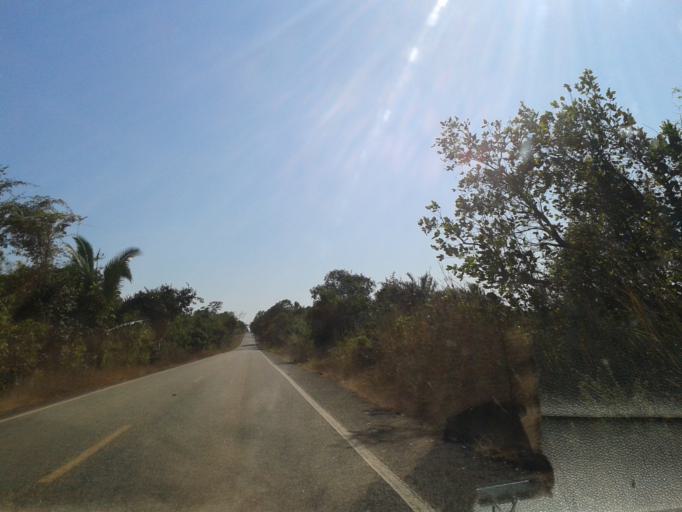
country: BR
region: Goias
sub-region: Mozarlandia
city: Mozarlandia
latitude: -14.6096
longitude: -50.5147
